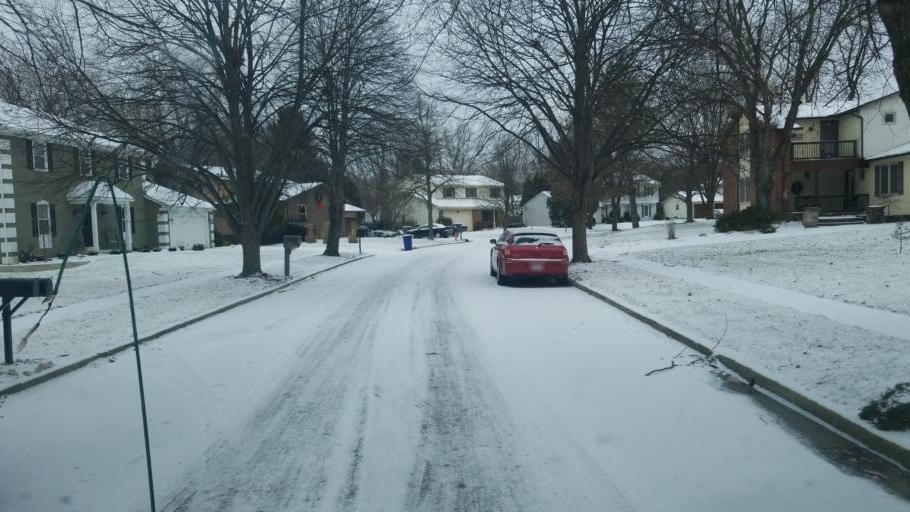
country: US
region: Ohio
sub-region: Delaware County
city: Powell
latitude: 40.1244
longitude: -83.0843
